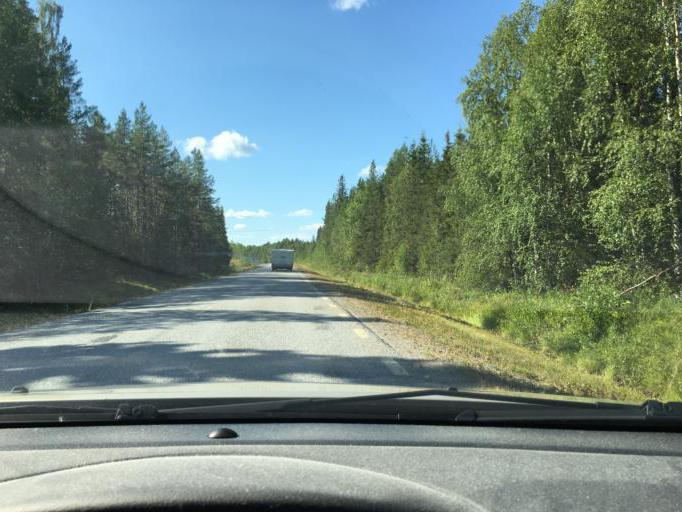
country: SE
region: Norrbotten
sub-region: Lulea Kommun
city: Ranea
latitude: 66.0466
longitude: 22.2809
